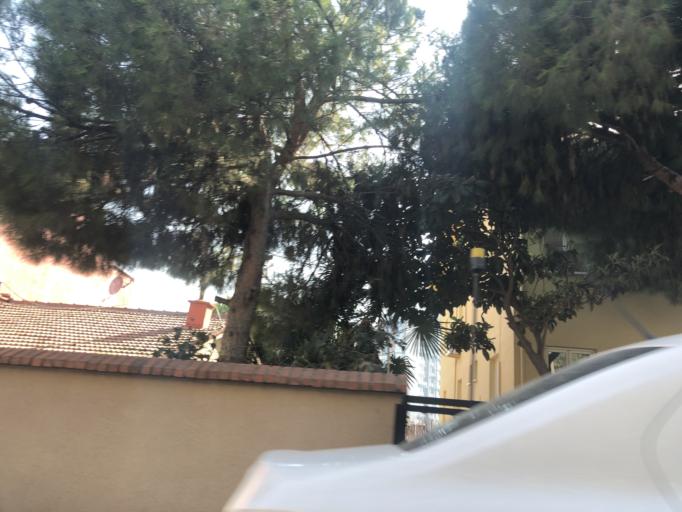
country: TR
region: Istanbul
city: UEskuedar
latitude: 41.0076
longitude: 29.0367
